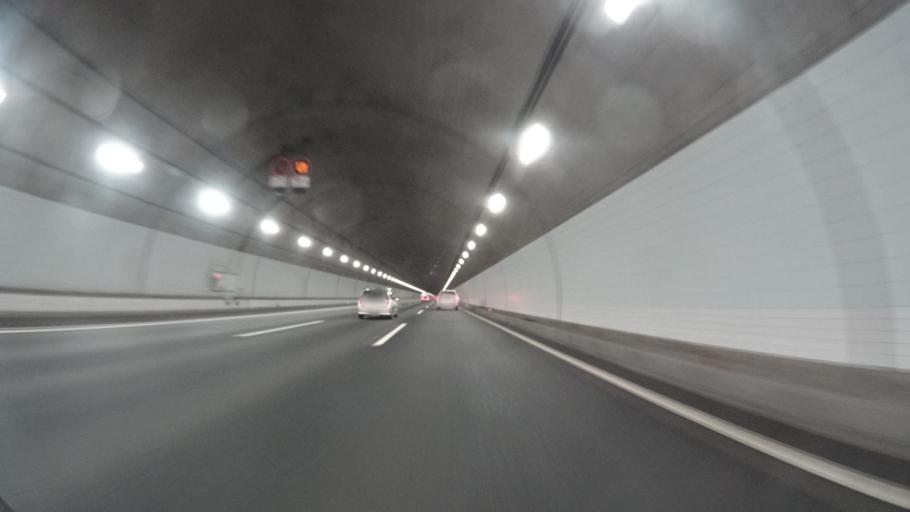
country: JP
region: Shizuoka
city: Kanaya
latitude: 34.8437
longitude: 138.0769
